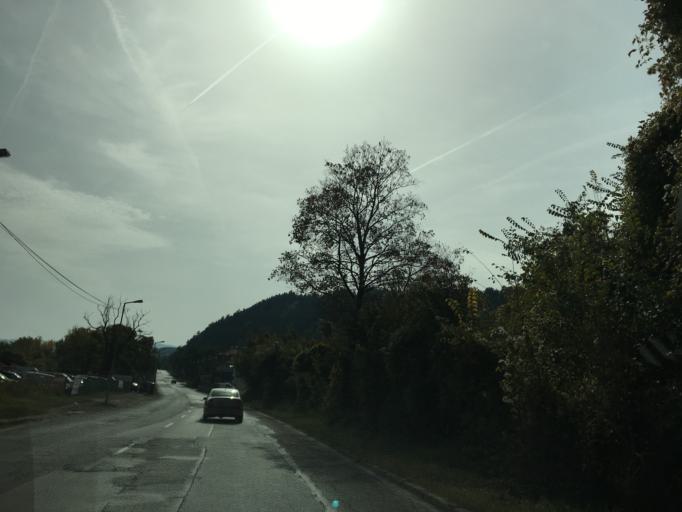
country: BG
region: Sofia-Capital
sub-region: Stolichna Obshtina
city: Sofia
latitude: 42.6096
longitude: 23.3995
